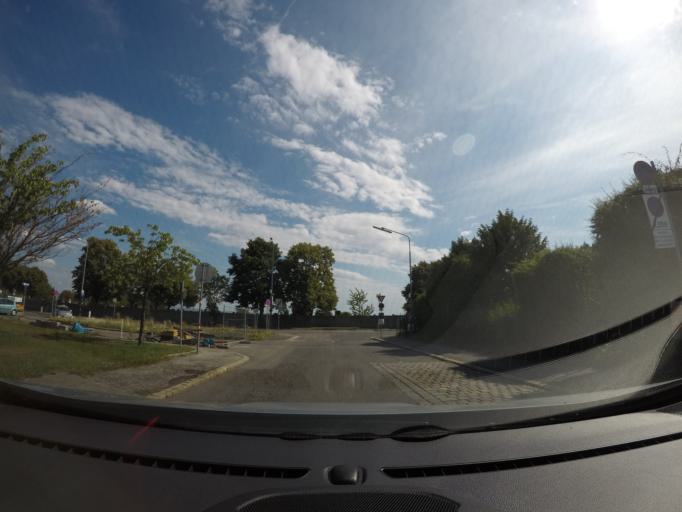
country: AT
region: Lower Austria
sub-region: Politischer Bezirk Modling
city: Perchtoldsdorf
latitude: 48.2048
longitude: 16.2812
